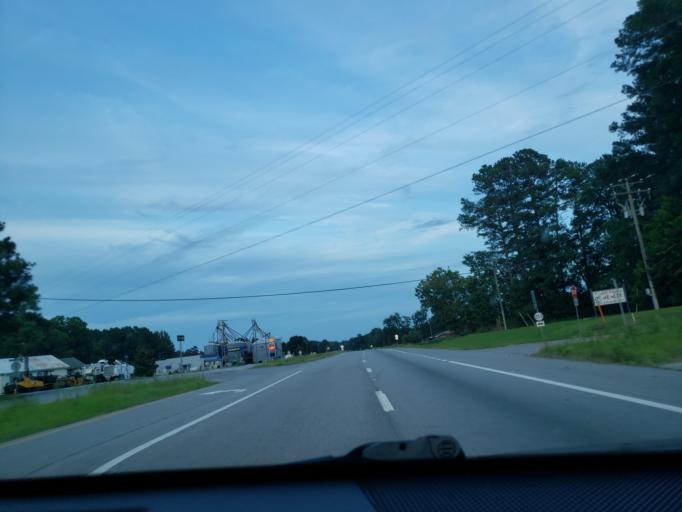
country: US
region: Virginia
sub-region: Southampton County
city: Courtland
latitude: 36.7058
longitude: -77.2034
